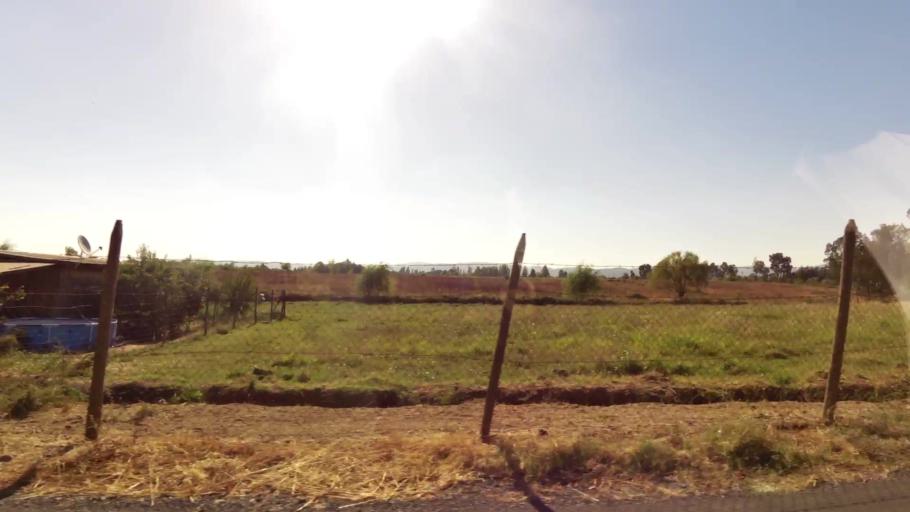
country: CL
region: Maule
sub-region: Provincia de Talca
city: Talca
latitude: -35.4102
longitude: -71.5919
